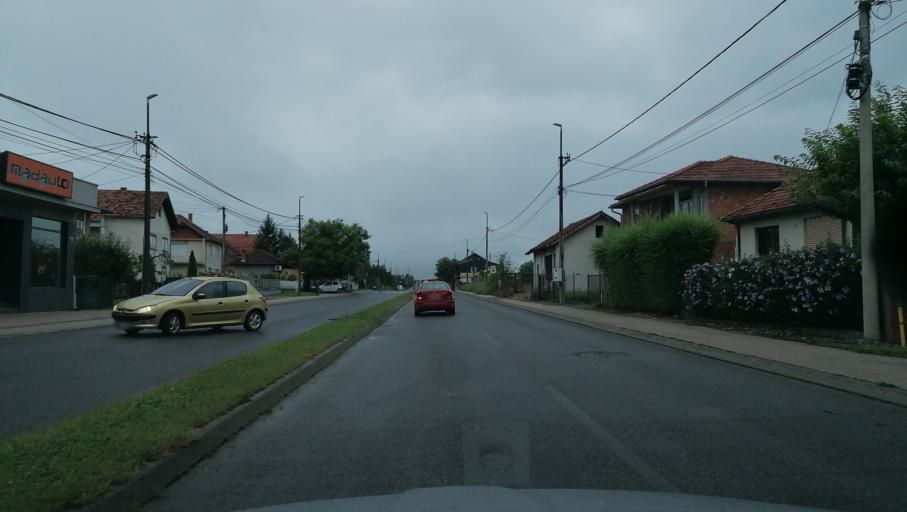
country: RS
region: Central Serbia
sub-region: Rasinski Okrug
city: Krusevac
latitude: 43.5861
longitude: 21.2944
